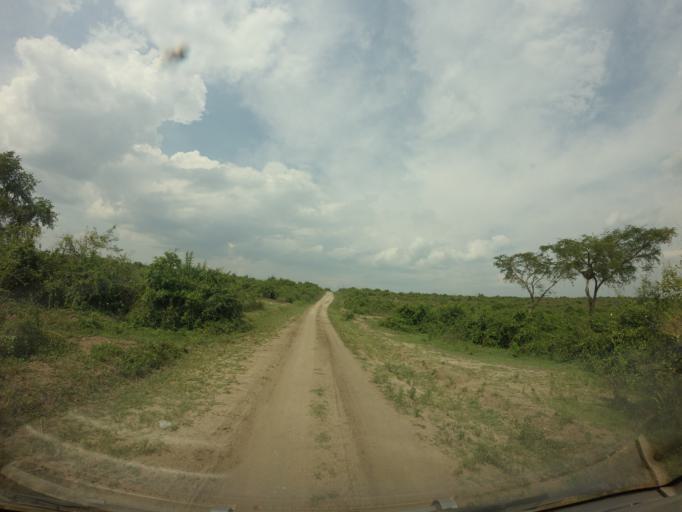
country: UG
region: Western Region
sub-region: Rubirizi District
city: Rubirizi
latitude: -0.2100
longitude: 29.9147
